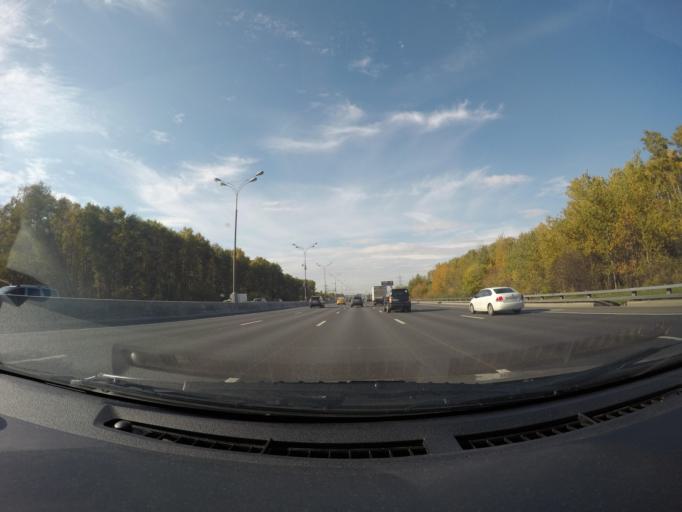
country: RU
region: Moscow
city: Vatutino
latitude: 55.8964
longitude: 37.6530
